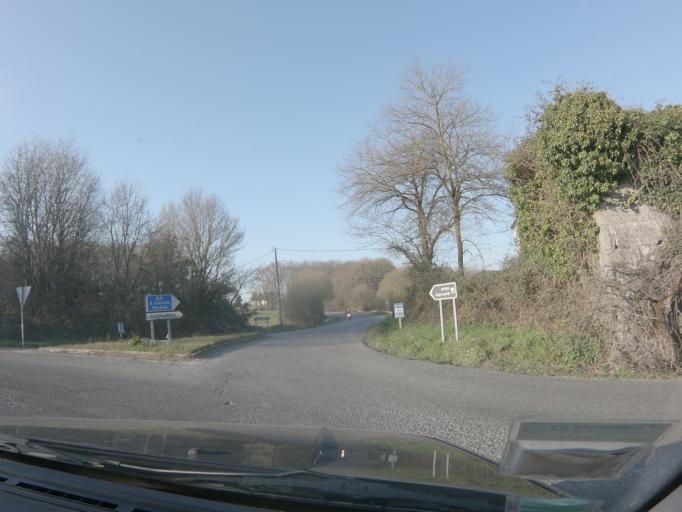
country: ES
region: Galicia
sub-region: Provincia de Lugo
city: Corgo
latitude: 42.9330
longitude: -7.3983
